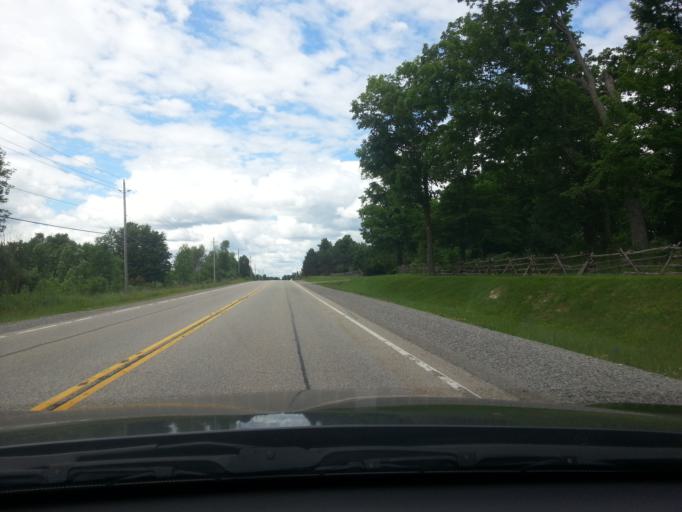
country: CA
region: Ontario
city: Perth
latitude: 44.7423
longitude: -76.1367
